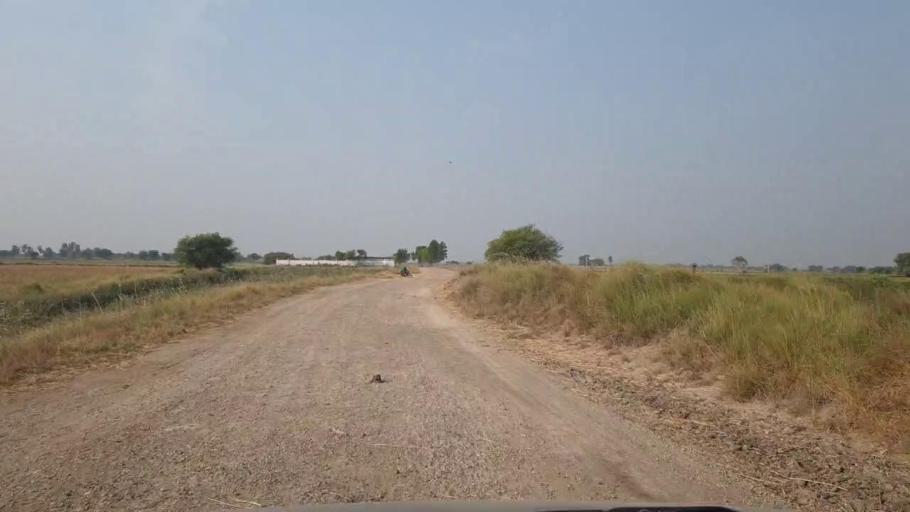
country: PK
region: Sindh
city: Tando Muhammad Khan
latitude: 25.1075
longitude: 68.5078
